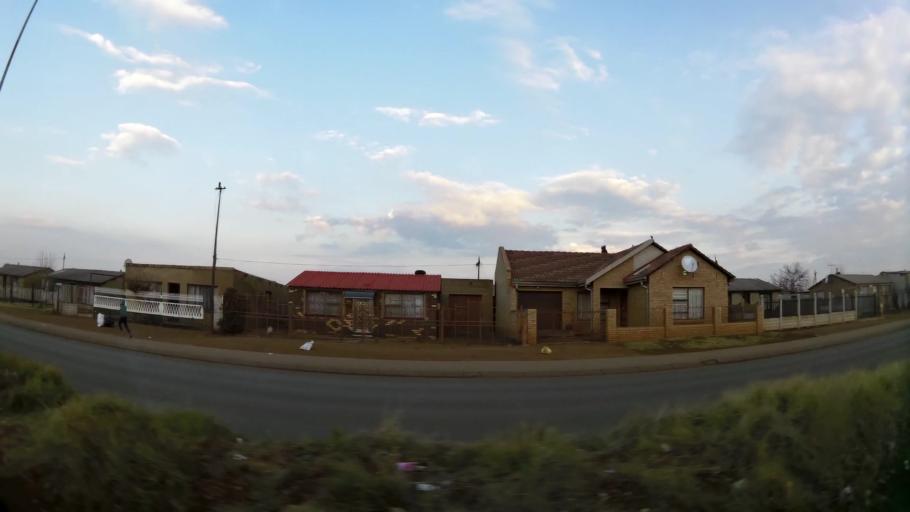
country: ZA
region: Gauteng
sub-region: City of Johannesburg Metropolitan Municipality
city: Orange Farm
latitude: -26.5685
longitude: 27.8476
